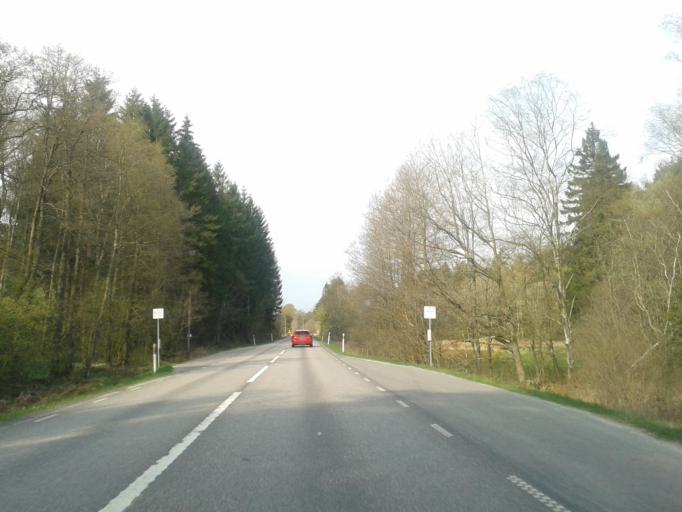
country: SE
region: Vaestra Goetaland
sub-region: Kungalvs Kommun
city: Kode
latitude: 57.8927
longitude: 11.8663
